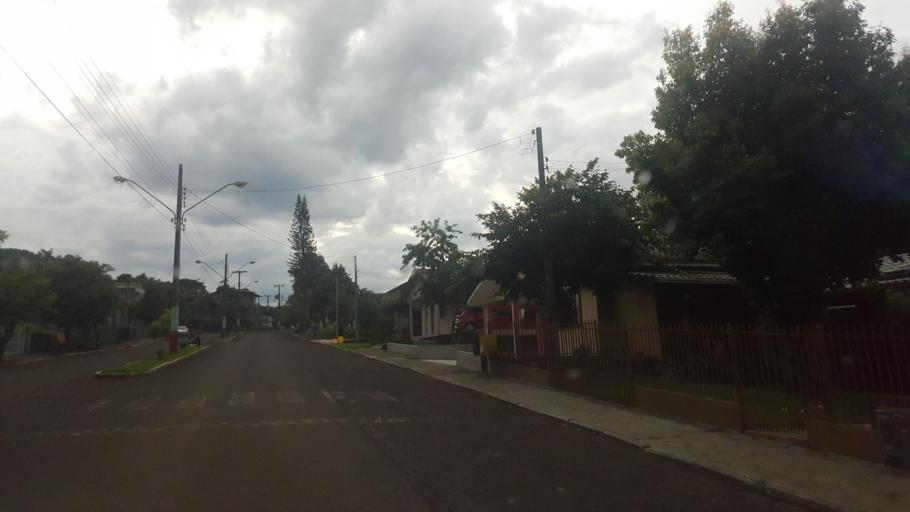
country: BR
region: Rio Grande do Sul
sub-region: Frederico Westphalen
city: Frederico Westphalen
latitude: -27.1061
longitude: -53.3958
